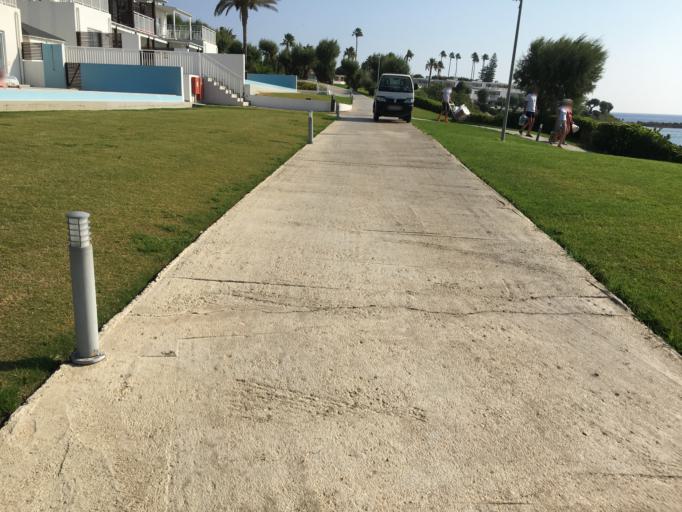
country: GR
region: South Aegean
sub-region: Nomos Dodekanisou
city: Rodos
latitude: 36.4051
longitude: 28.2280
